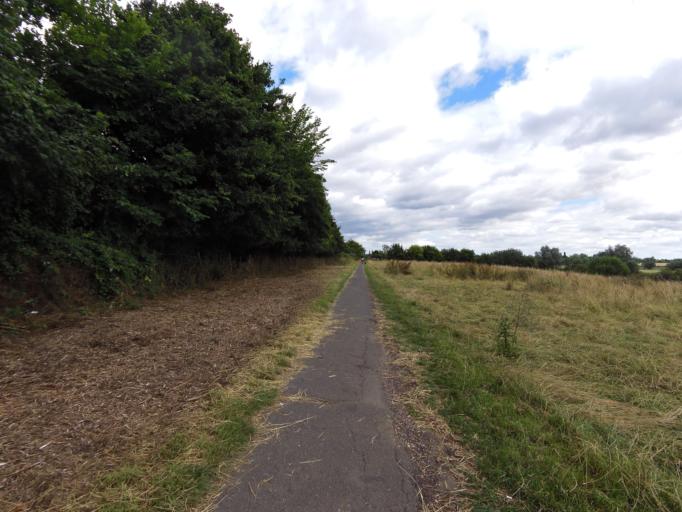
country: GB
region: England
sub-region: Cambridgeshire
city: Grantchester
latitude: 52.1804
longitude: 0.0967
